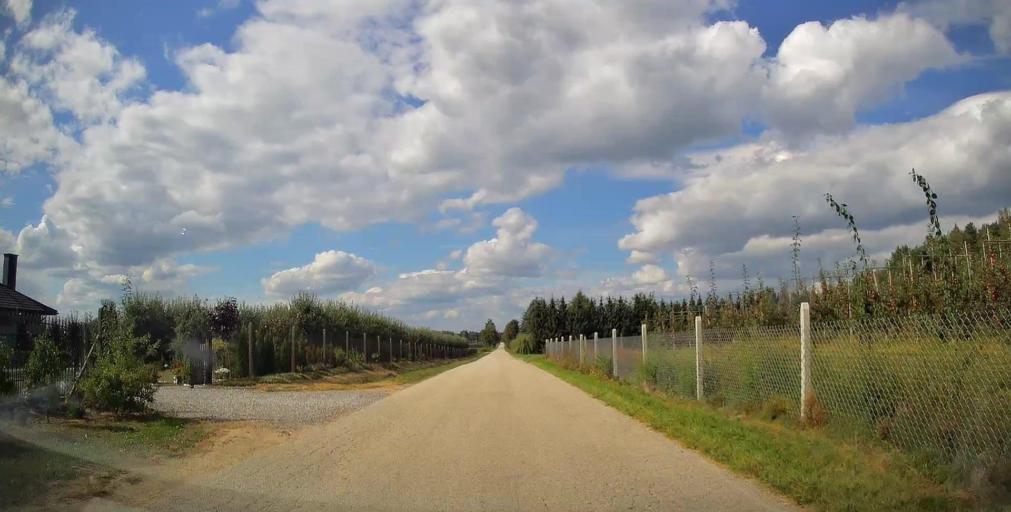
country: PL
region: Masovian Voivodeship
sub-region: Powiat grojecki
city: Goszczyn
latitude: 51.7043
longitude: 20.8962
